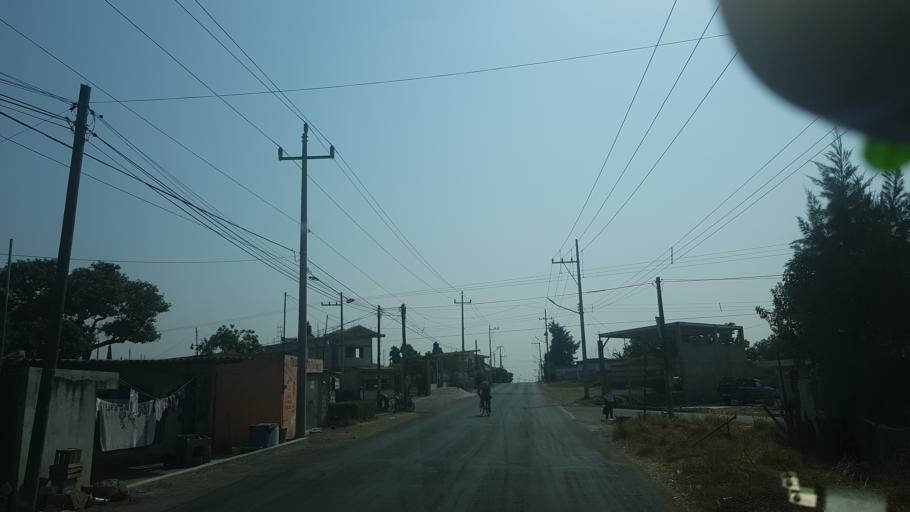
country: MX
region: Puebla
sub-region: San Jeronimo Tecuanipan
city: Los Reyes Tlanechicolpan
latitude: 19.0539
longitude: -98.3378
